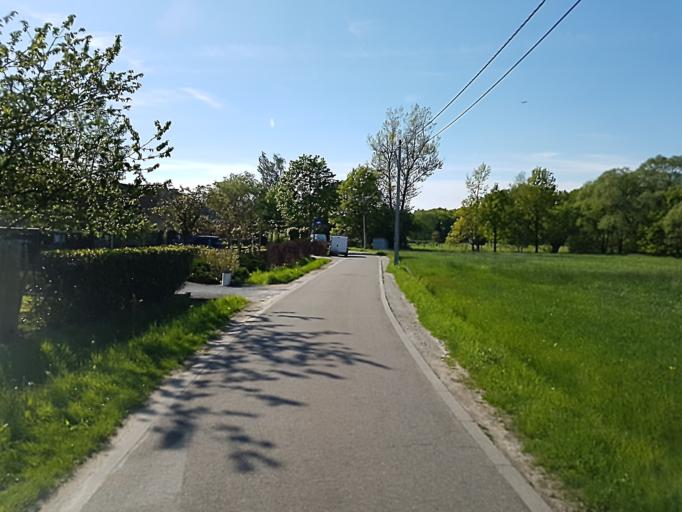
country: BE
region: Flanders
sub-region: Provincie Vlaams-Brabant
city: Boortmeerbeek
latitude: 51.0080
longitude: 4.5824
